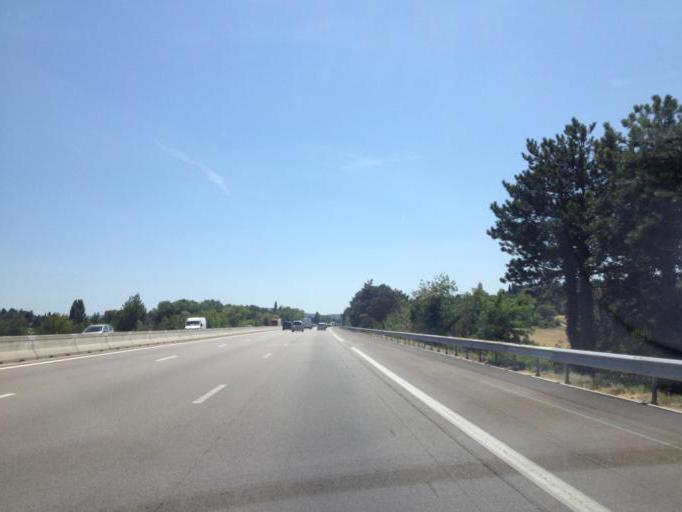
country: FR
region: Rhone-Alpes
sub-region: Departement de la Drome
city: Montboucher-sur-Jabron
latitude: 44.5622
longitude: 4.8110
